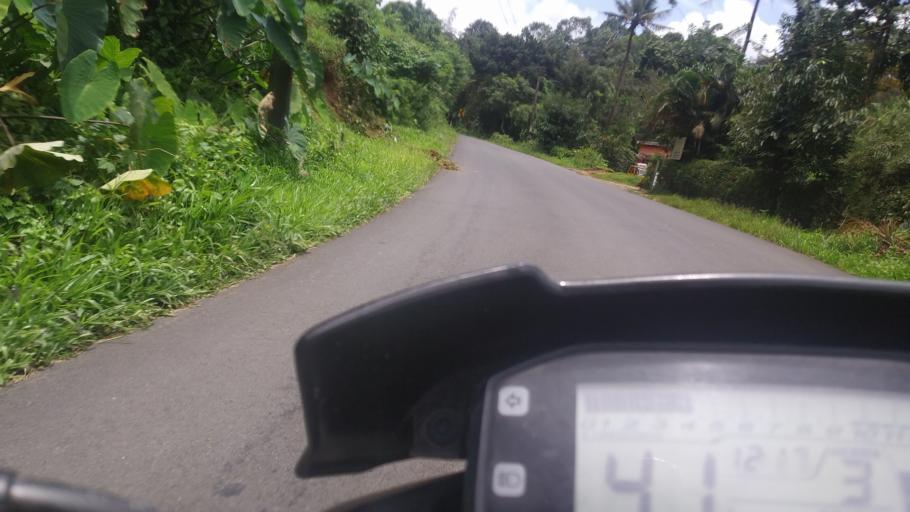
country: IN
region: Kerala
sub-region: Idukki
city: Munnar
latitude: 10.0178
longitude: 77.0105
